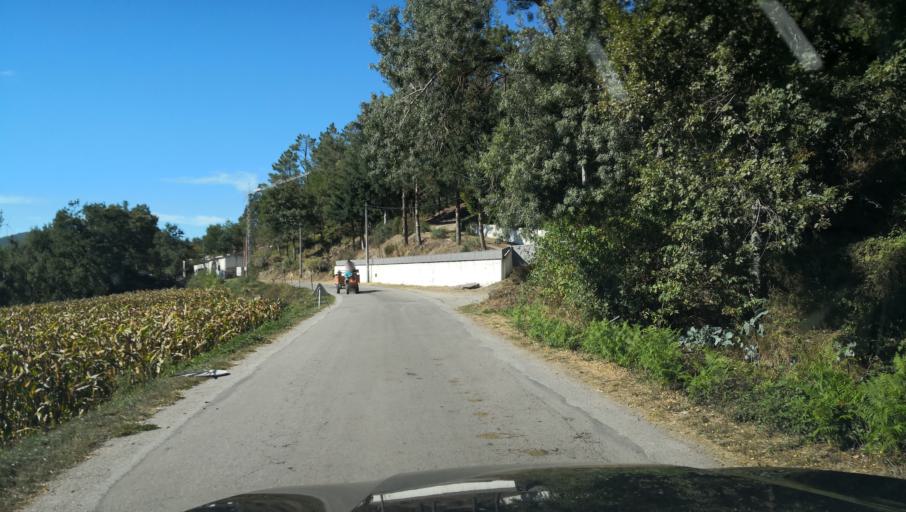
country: PT
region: Vila Real
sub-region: Santa Marta de Penaguiao
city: Santa Marta de Penaguiao
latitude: 41.2889
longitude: -7.8534
